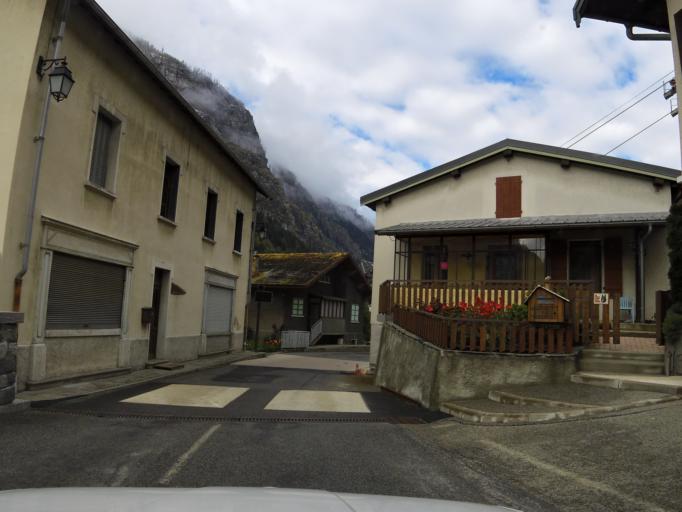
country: FR
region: Rhone-Alpes
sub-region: Departement de la Savoie
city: Saint-Michel-de-Maurienne
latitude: 45.2080
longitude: 6.5471
